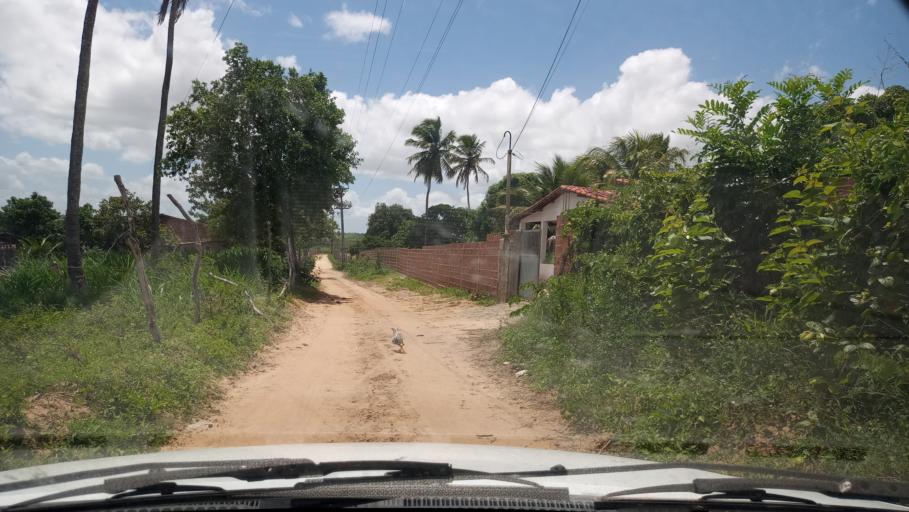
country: BR
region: Rio Grande do Norte
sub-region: Brejinho
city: Brejinho
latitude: -6.2619
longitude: -35.3734
